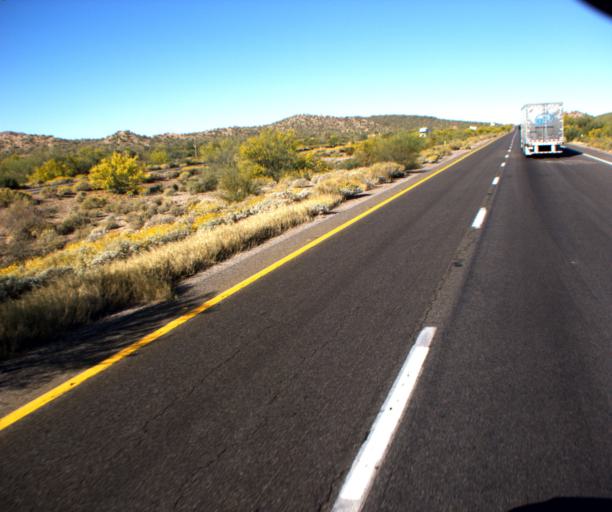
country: US
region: Arizona
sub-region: Pinal County
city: Maricopa
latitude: 32.8349
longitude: -112.1385
